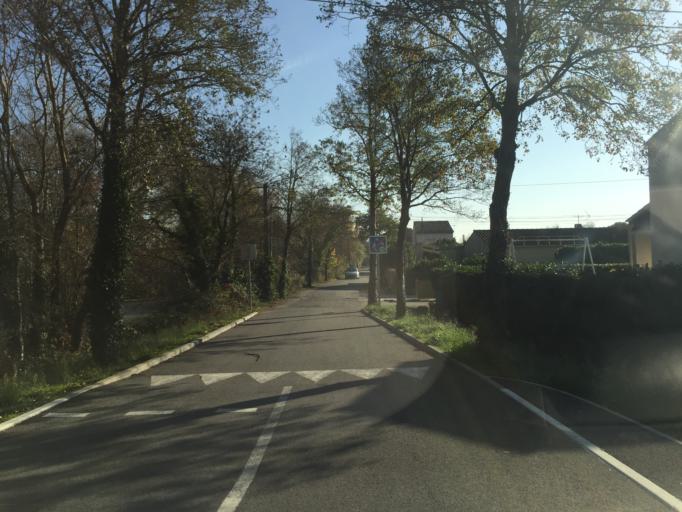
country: FR
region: Provence-Alpes-Cote d'Azur
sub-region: Departement du Vaucluse
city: Entraigues-sur-la-Sorgue
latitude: 44.0071
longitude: 4.9286
